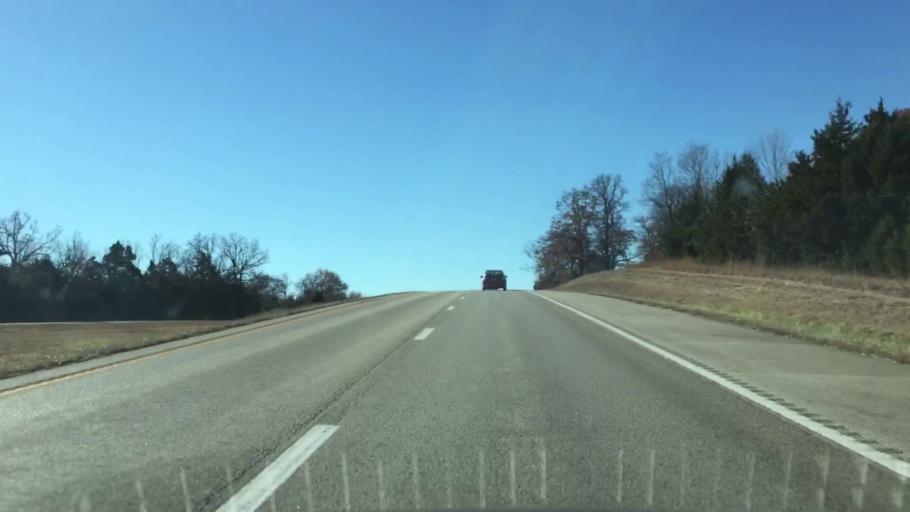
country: US
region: Missouri
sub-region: Cole County
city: Wardsville
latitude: 38.4561
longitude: -92.2988
